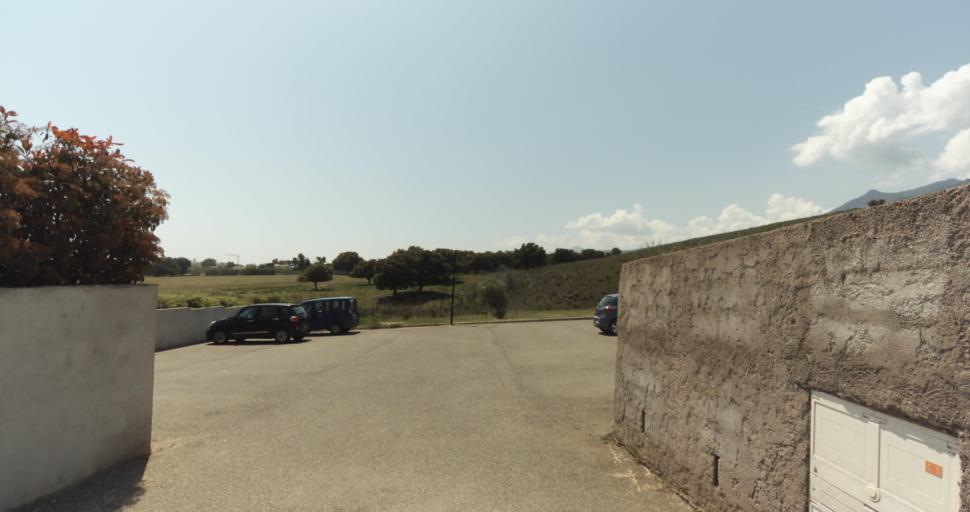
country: FR
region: Corsica
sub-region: Departement de la Haute-Corse
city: Biguglia
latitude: 42.5995
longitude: 9.4308
